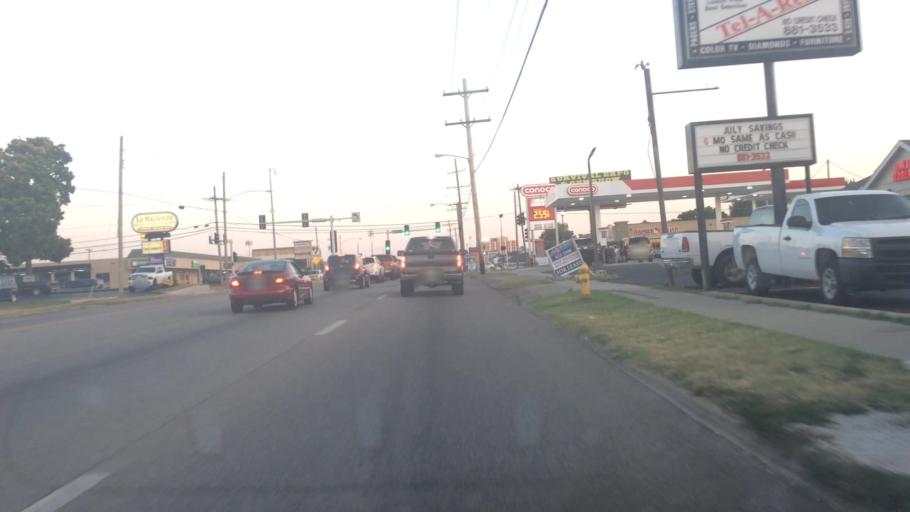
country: US
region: Missouri
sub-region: Greene County
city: Springfield
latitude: 37.1898
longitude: -93.2623
